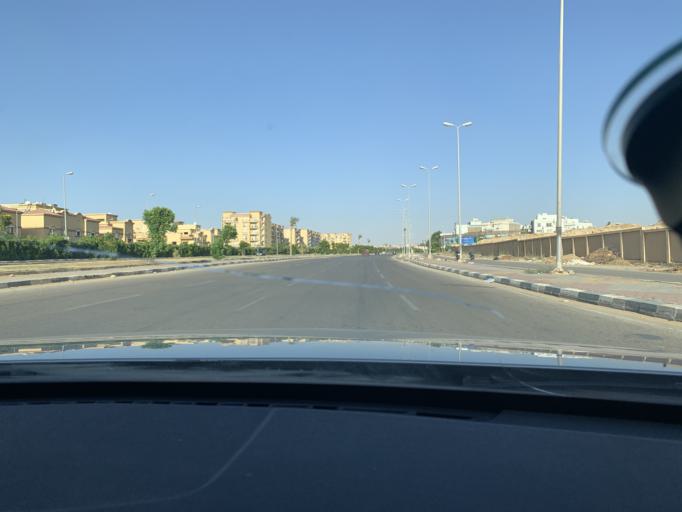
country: EG
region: Muhafazat al Qalyubiyah
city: Al Khankah
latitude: 30.0530
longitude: 31.5032
